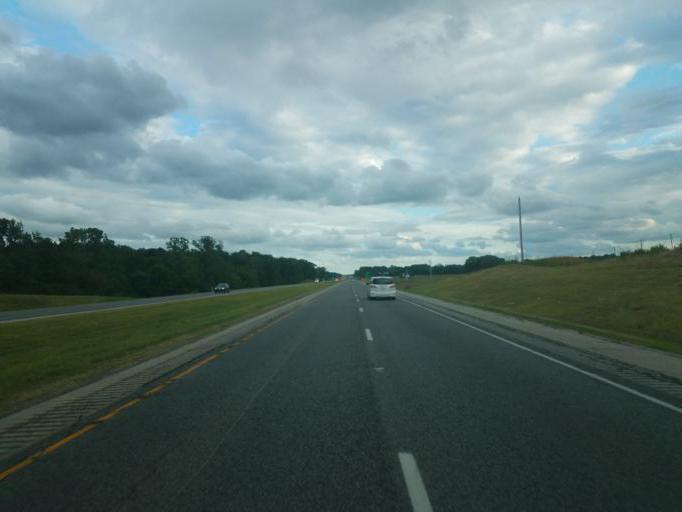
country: US
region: Indiana
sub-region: DeKalb County
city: Waterloo
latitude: 41.4557
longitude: -85.0541
